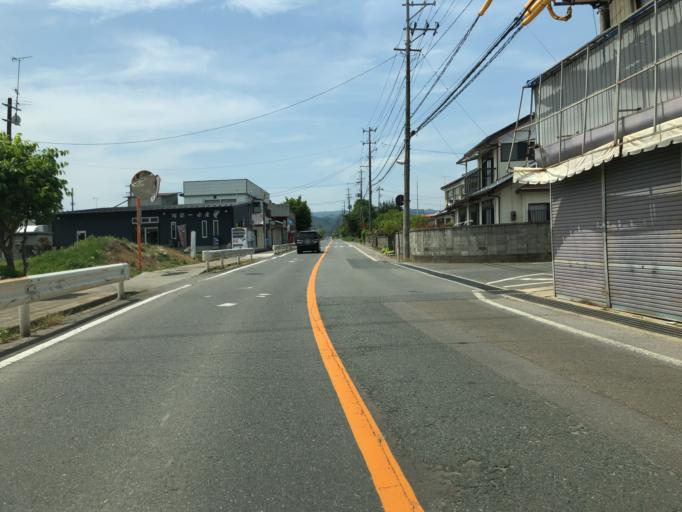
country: JP
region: Fukushima
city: Namie
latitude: 37.6970
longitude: 140.9562
